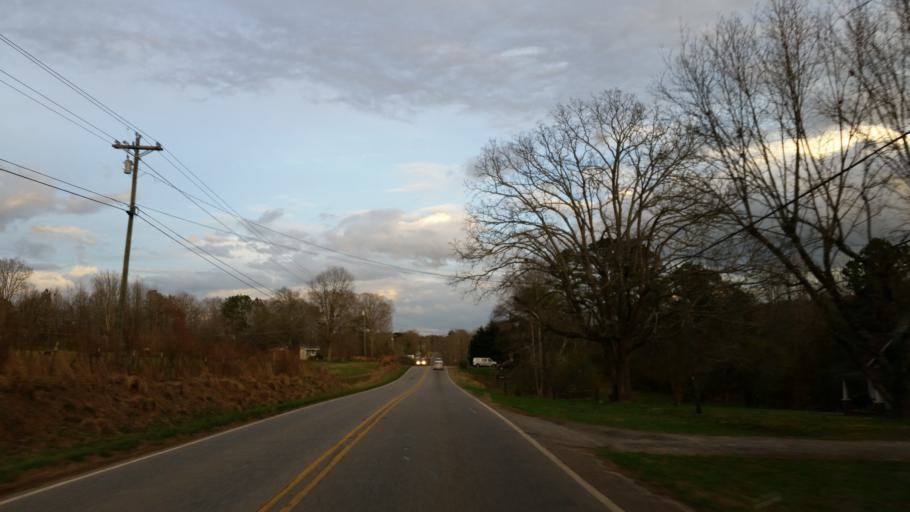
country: US
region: Georgia
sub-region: Pickens County
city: Jasper
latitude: 34.4687
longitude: -84.4998
